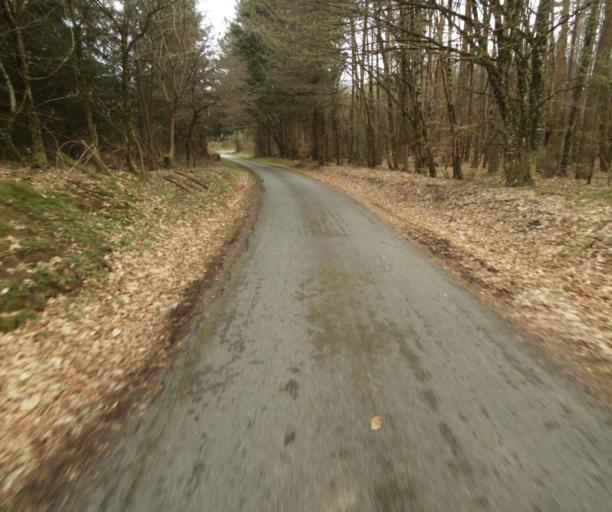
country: FR
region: Limousin
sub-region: Departement de la Correze
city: Argentat
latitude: 45.1927
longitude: 1.9285
